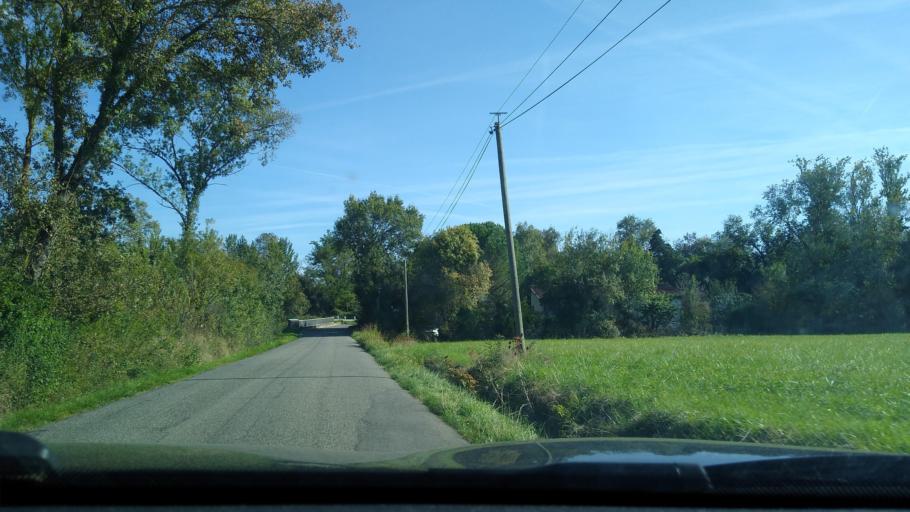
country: FR
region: Midi-Pyrenees
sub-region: Departement de la Haute-Garonne
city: Montaigut-sur-Save
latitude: 43.7285
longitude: 1.2430
